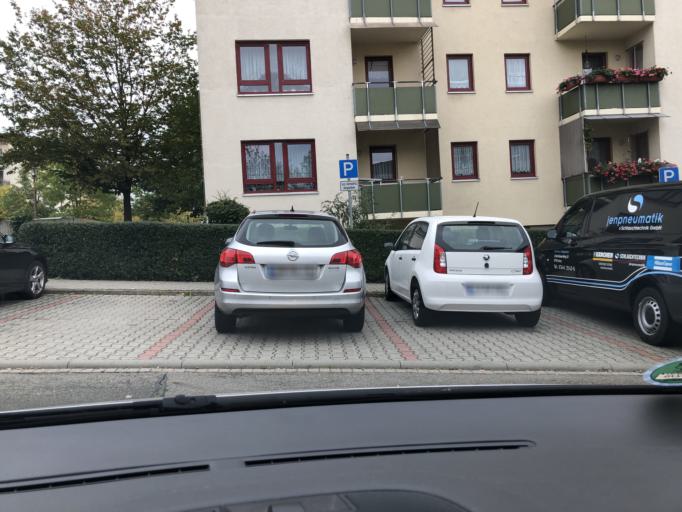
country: DE
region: Thuringia
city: Gera
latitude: 50.9016
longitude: 12.0967
